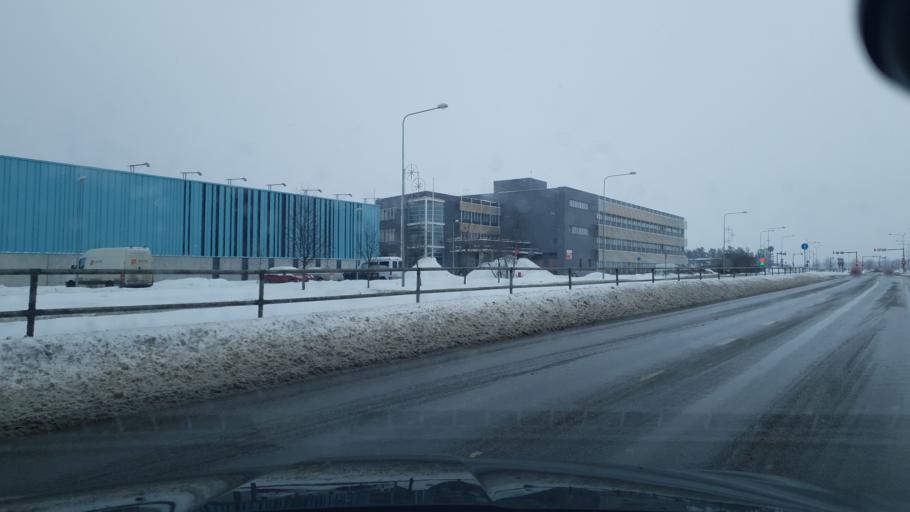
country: EE
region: Harju
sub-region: Tallinna linn
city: Kose
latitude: 59.4386
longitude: 24.8702
